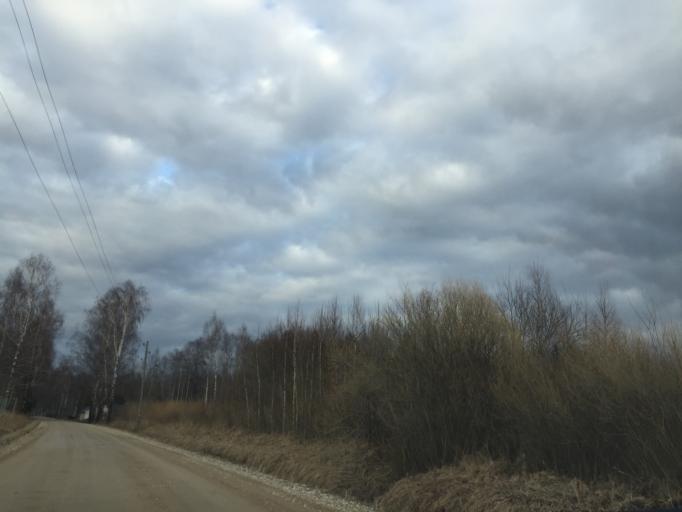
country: LV
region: Jaunjelgava
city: Jaunjelgava
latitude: 56.5994
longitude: 25.0596
